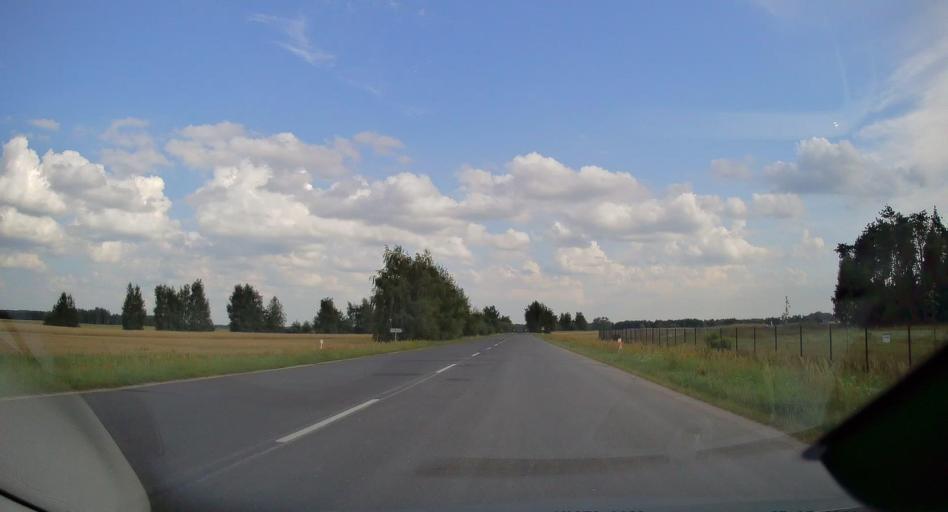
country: PL
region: Lodz Voivodeship
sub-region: Powiat tomaszowski
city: Rzeczyca
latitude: 51.6511
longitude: 20.2789
